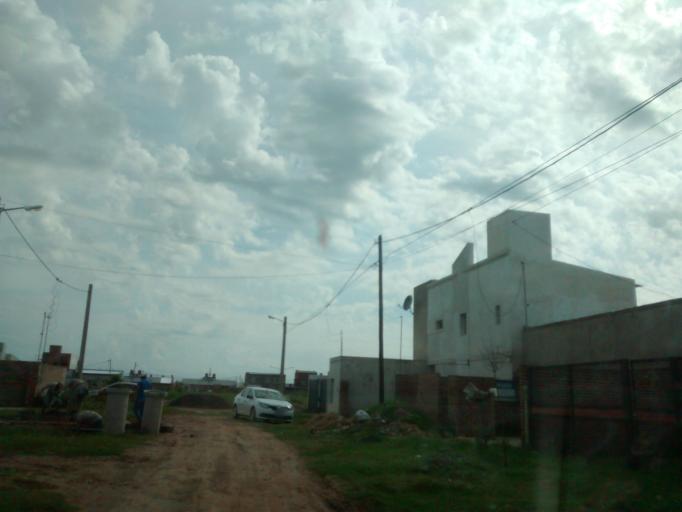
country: AR
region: Chaco
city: Resistencia
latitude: -27.4066
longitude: -58.9666
